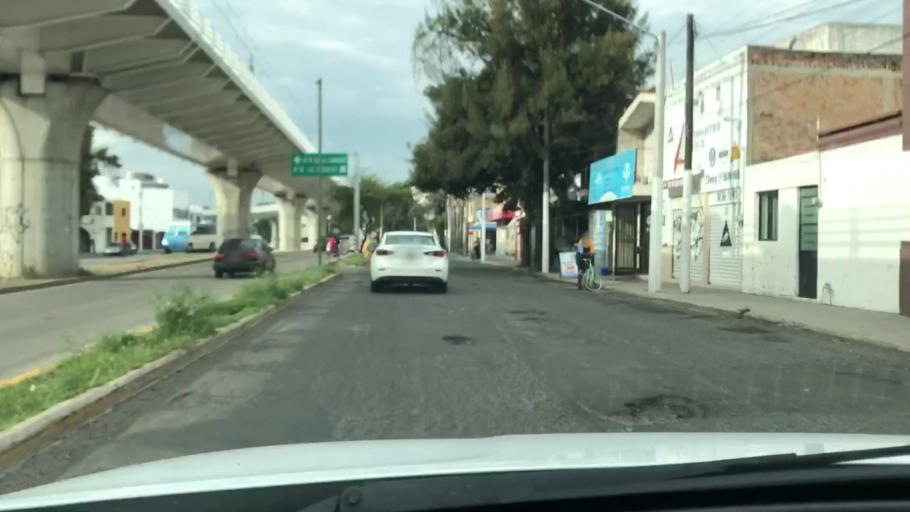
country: MX
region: Jalisco
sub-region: Zapopan
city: Zapopan
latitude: 20.7242
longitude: -103.3874
